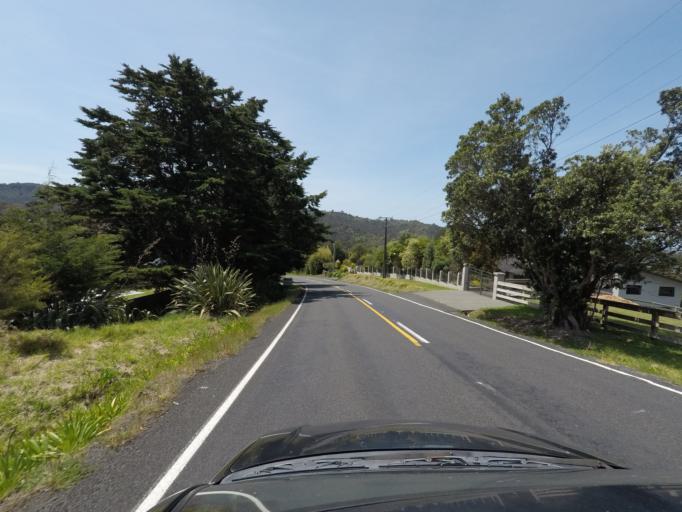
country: NZ
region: Auckland
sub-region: Auckland
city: Titirangi
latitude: -36.9765
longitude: 174.6135
